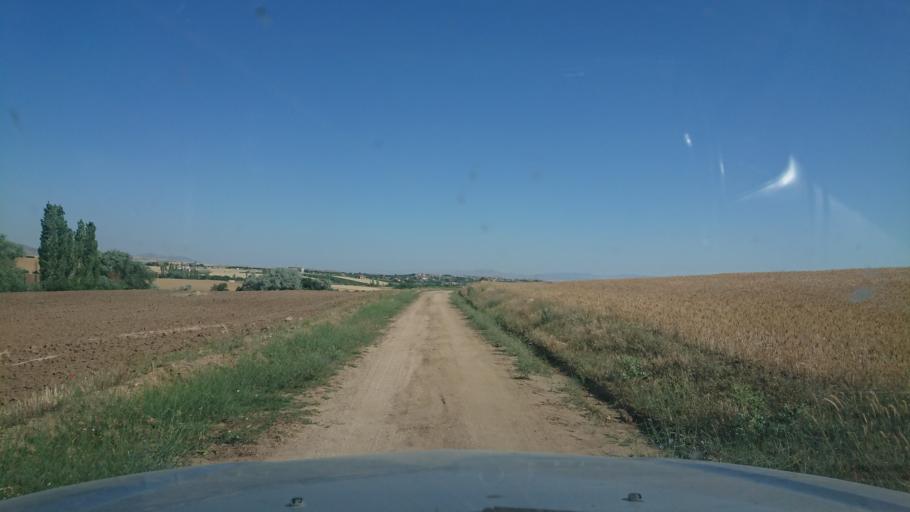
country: TR
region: Aksaray
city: Agacoren
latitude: 38.8517
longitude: 33.9148
